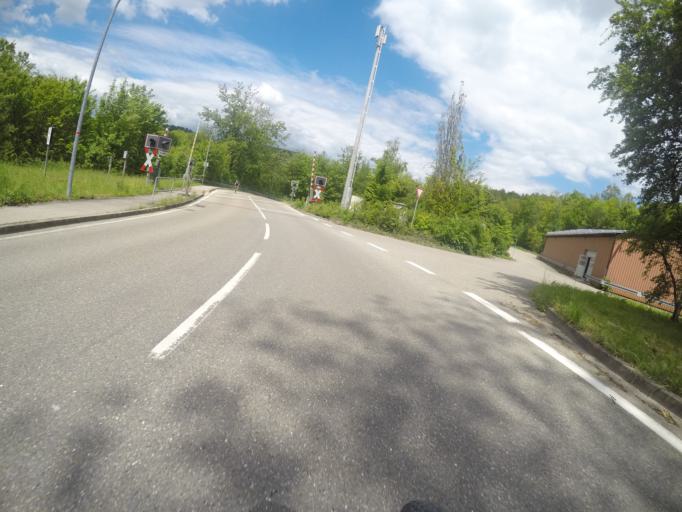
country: DE
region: Baden-Wuerttemberg
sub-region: Karlsruhe Region
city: Nagold
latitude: 48.5868
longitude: 8.7335
